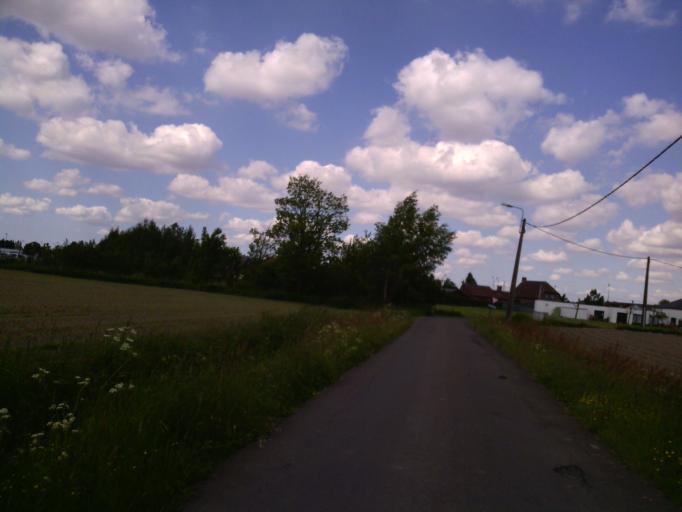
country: BE
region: Flanders
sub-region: Provincie West-Vlaanderen
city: Wevelgem
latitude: 50.7876
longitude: 3.1523
